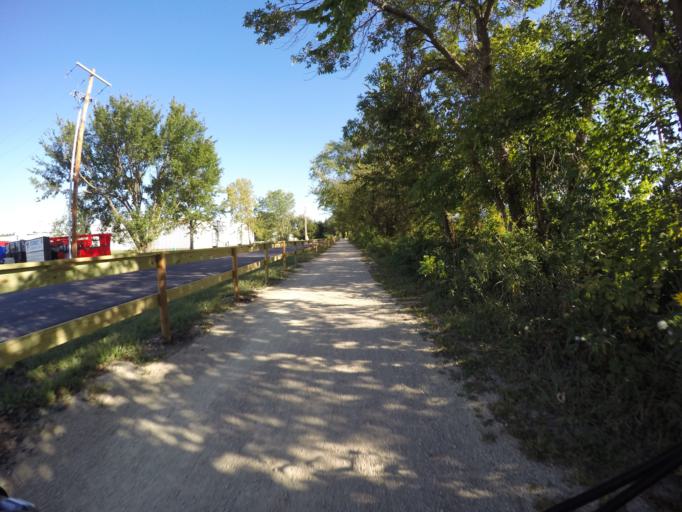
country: US
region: Kansas
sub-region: Riley County
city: Manhattan
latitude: 39.1825
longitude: -96.6080
